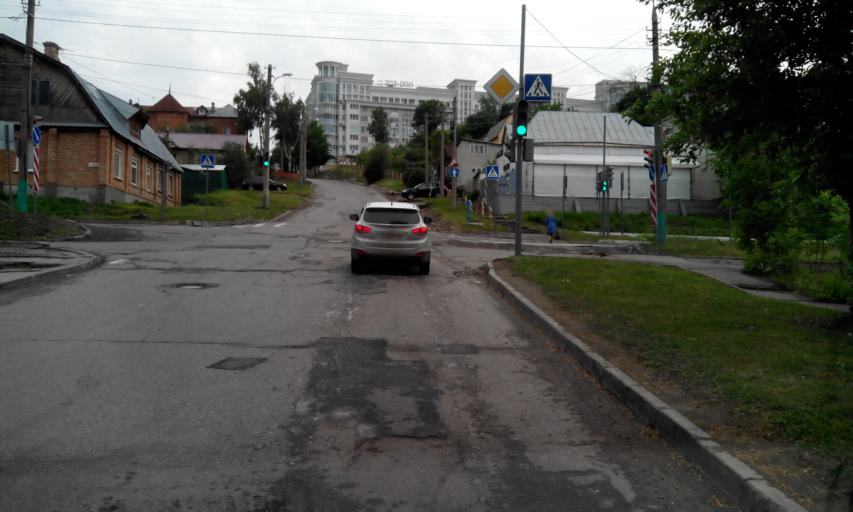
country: RU
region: Penza
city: Penza
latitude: 53.1912
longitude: 45.0089
